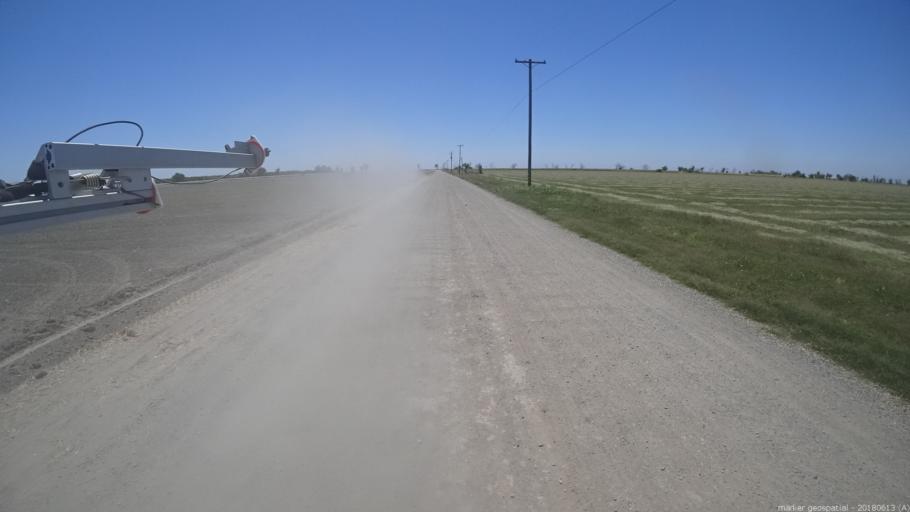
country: US
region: California
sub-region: Madera County
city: Chowchilla
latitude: 37.0017
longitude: -120.3465
